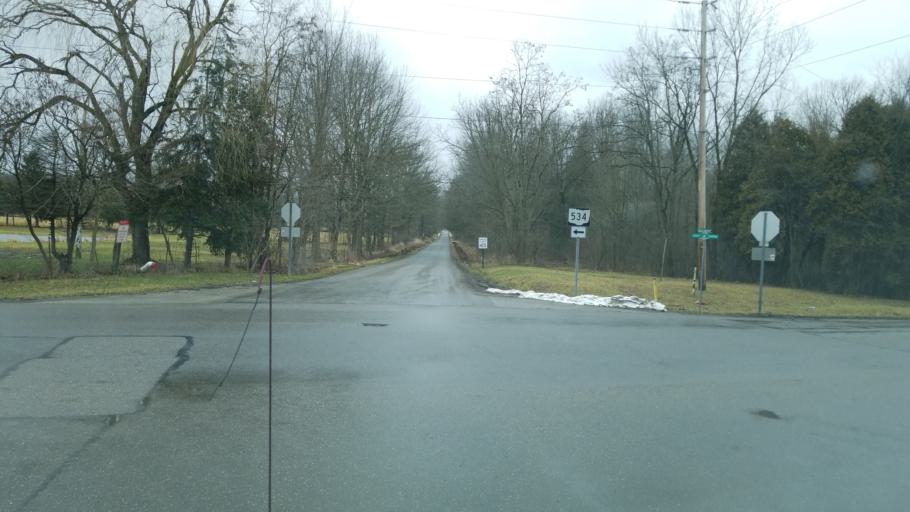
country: US
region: Ohio
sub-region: Trumbull County
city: Leavittsburg
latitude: 41.3394
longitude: -80.9578
